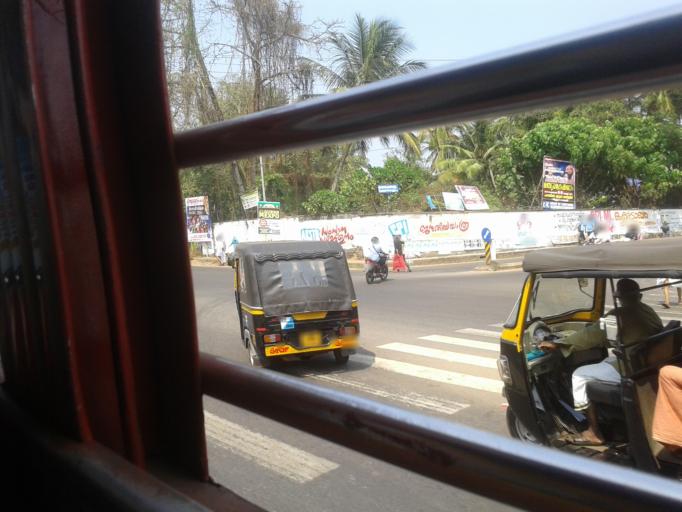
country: IN
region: Kerala
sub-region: Kozhikode
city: Badagara
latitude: 11.6007
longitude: 75.5925
